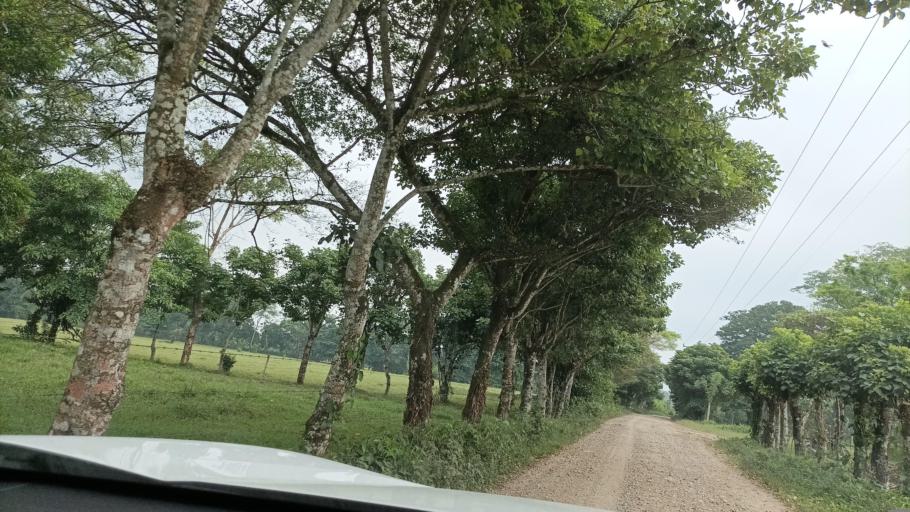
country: MX
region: Veracruz
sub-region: Uxpanapa
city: Poblado 10
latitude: 17.5481
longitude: -94.2292
